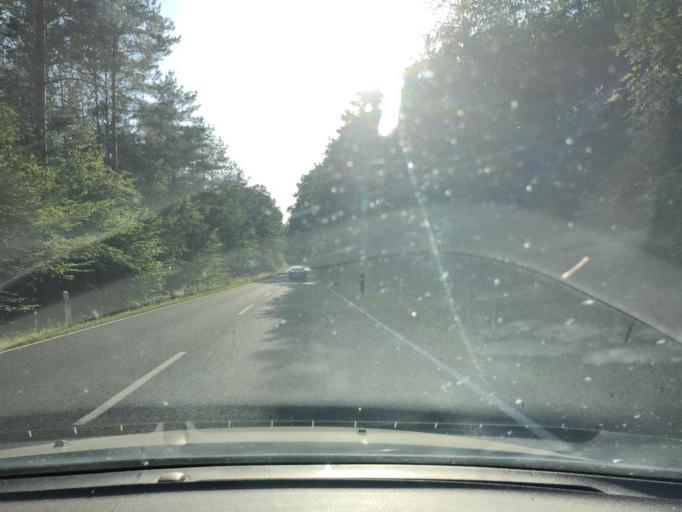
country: DE
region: Saxony
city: Wermsdorf
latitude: 51.3349
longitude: 12.9093
